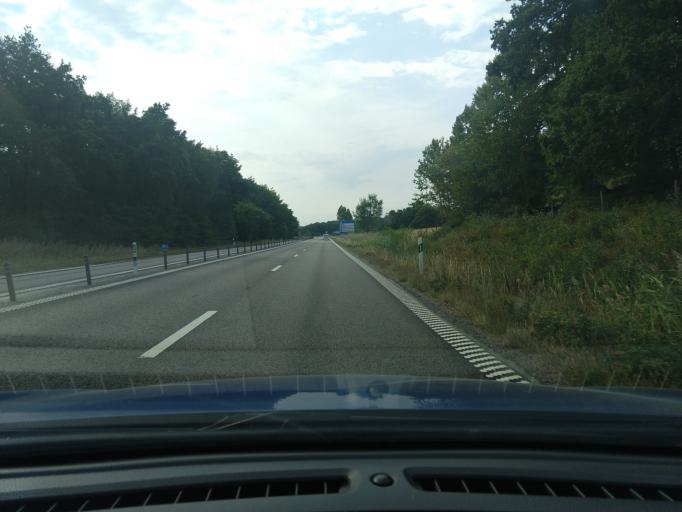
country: SE
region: Blekinge
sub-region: Karlskrona Kommun
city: Rodeby
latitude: 56.2002
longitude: 15.6773
